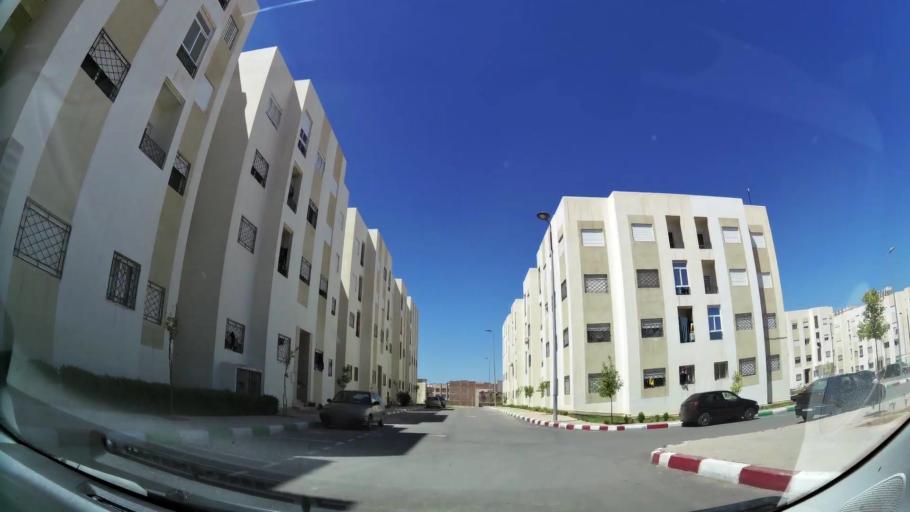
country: MA
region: Oriental
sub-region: Oujda-Angad
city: Oujda
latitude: 34.6531
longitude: -1.8806
